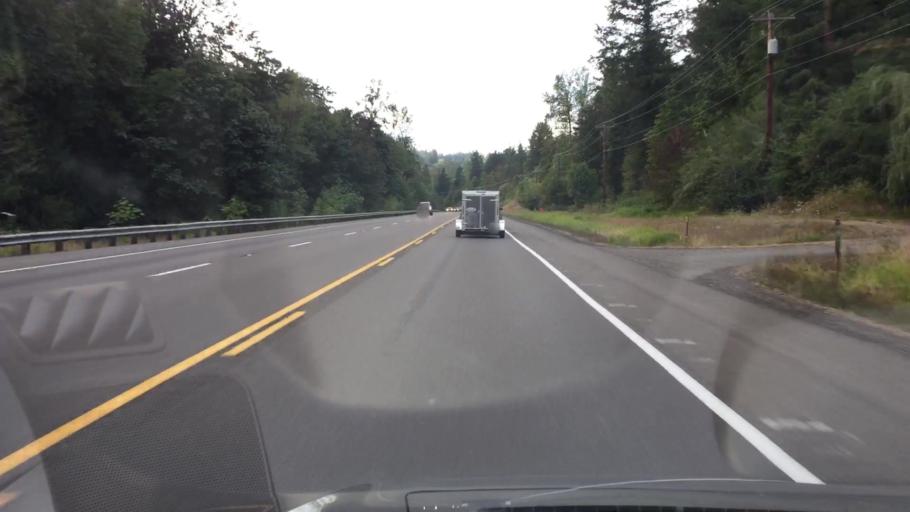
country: US
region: Washington
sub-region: Lewis County
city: Napavine
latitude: 46.5302
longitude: -122.6070
